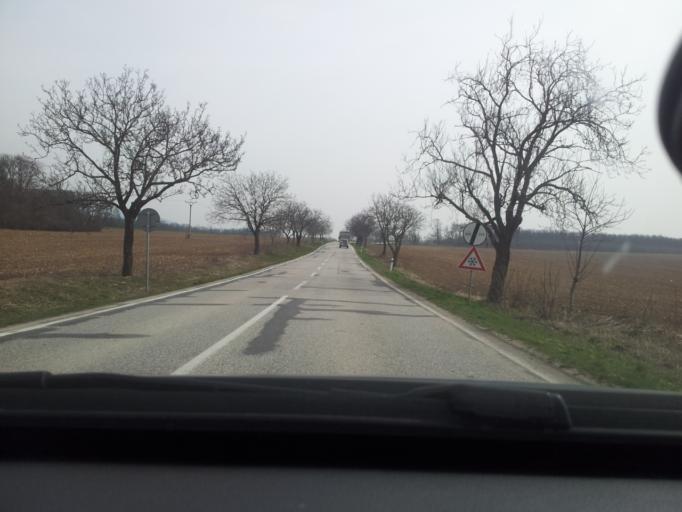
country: SK
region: Nitriansky
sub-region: Okres Nitra
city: Nitra
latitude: 48.3395
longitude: 17.9888
